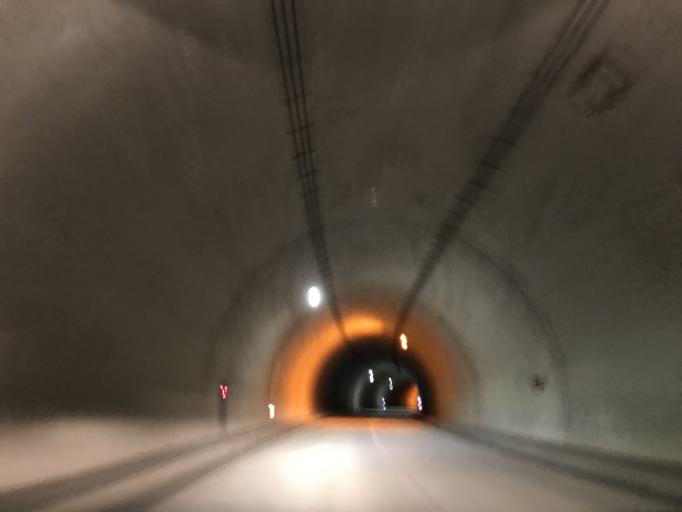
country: JP
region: Iwate
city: Mizusawa
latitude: 39.0269
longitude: 141.0196
